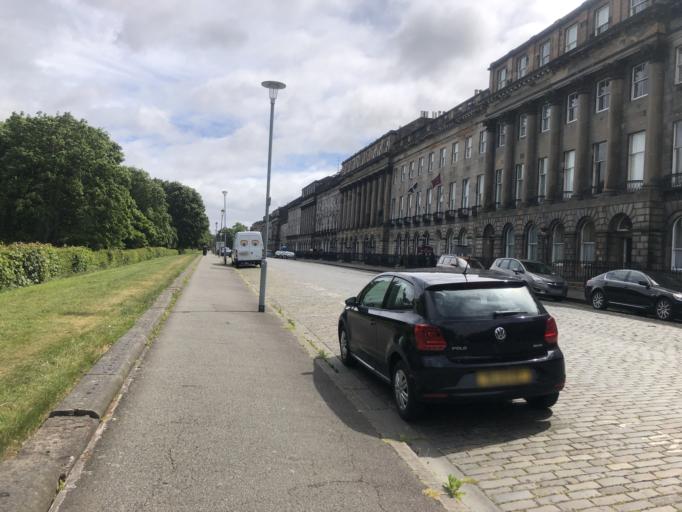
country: GB
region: Scotland
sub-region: Edinburgh
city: Edinburgh
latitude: 55.9570
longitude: -3.1794
